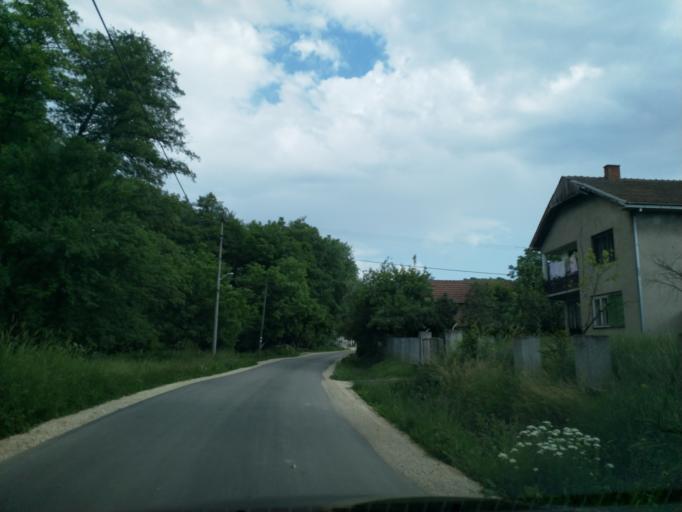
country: RS
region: Central Serbia
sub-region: Borski Okrug
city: Bor
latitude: 44.0196
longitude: 21.9807
